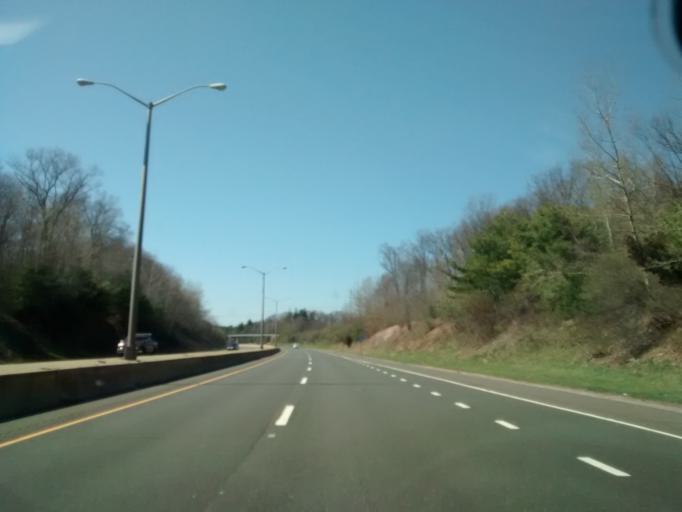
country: US
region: Connecticut
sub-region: Hartford County
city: East Hartford
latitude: 41.7976
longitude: -72.5776
